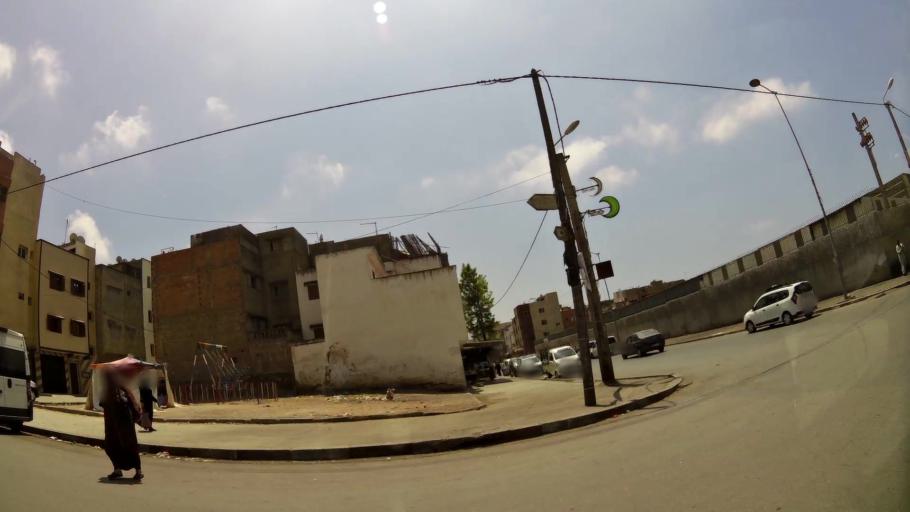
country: MA
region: Rabat-Sale-Zemmour-Zaer
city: Sale
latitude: 34.0619
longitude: -6.7936
